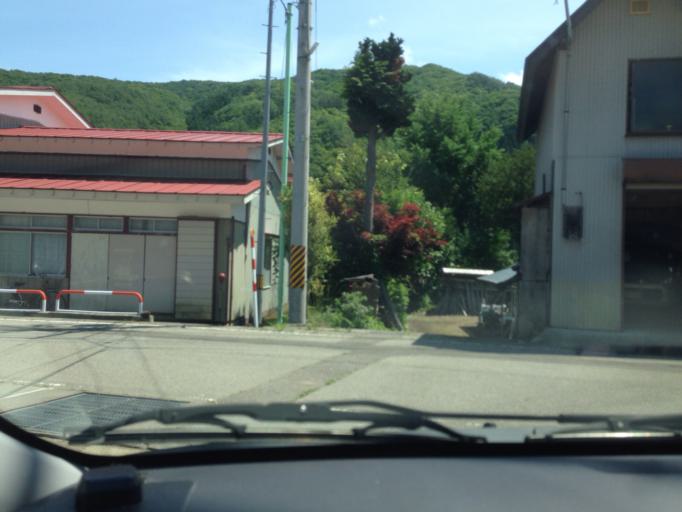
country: JP
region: Tochigi
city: Kuroiso
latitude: 37.2045
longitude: 139.7288
